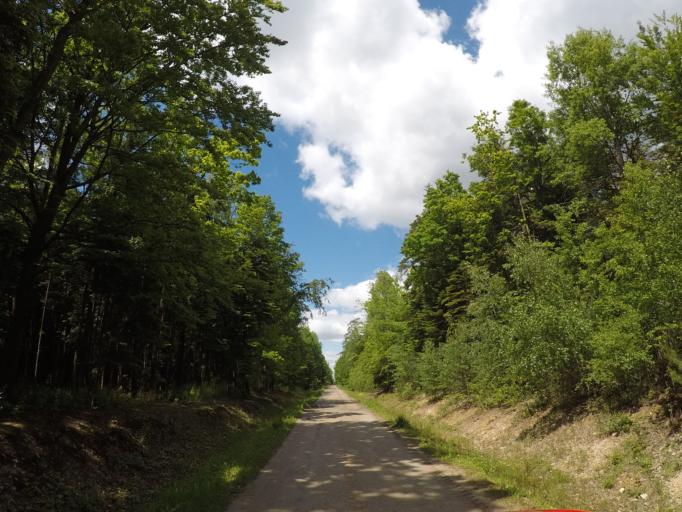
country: PL
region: Swietokrzyskie
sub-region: Powiat kielecki
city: Domaszowice
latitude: 50.9122
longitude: 20.6556
